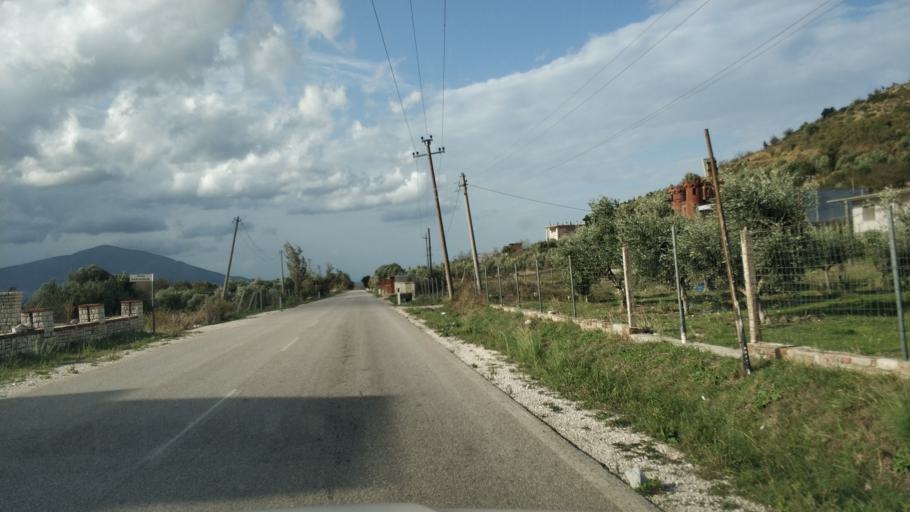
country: AL
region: Vlore
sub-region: Rrethi i Vlores
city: Orikum
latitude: 40.2993
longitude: 19.4865
